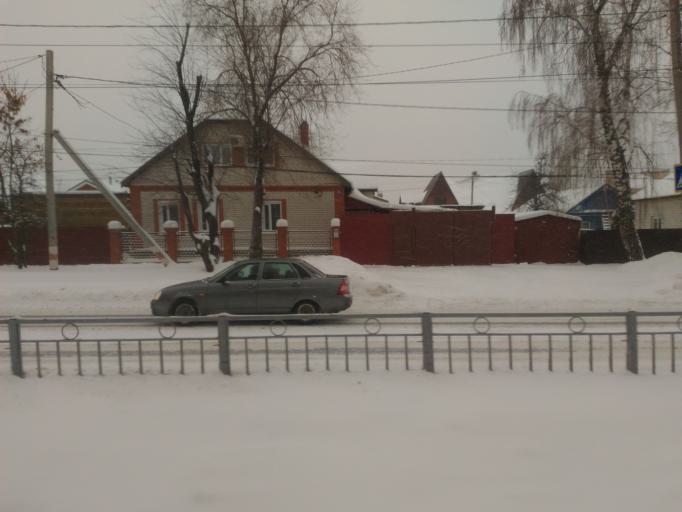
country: RU
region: Ulyanovsk
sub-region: Ulyanovskiy Rayon
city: Ulyanovsk
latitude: 54.3556
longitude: 48.3772
